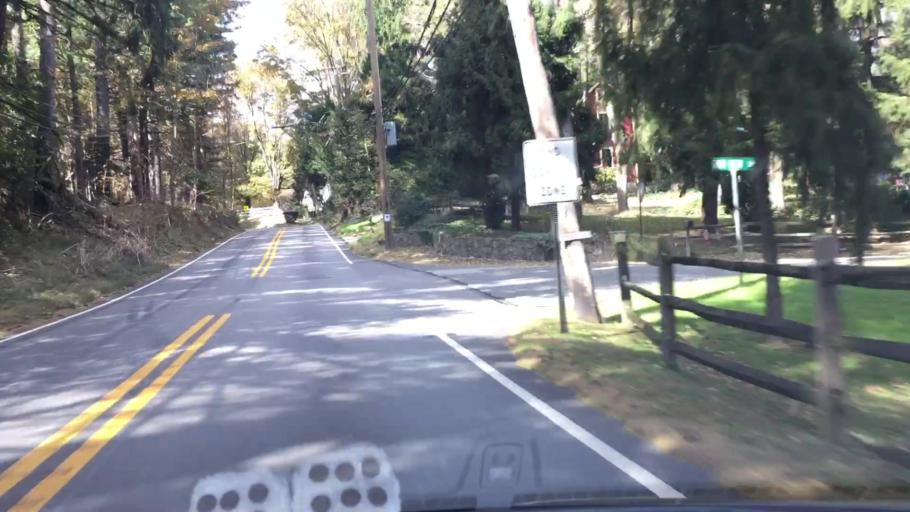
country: US
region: Pennsylvania
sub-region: Delaware County
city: Media
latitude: 39.9447
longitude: -75.3986
